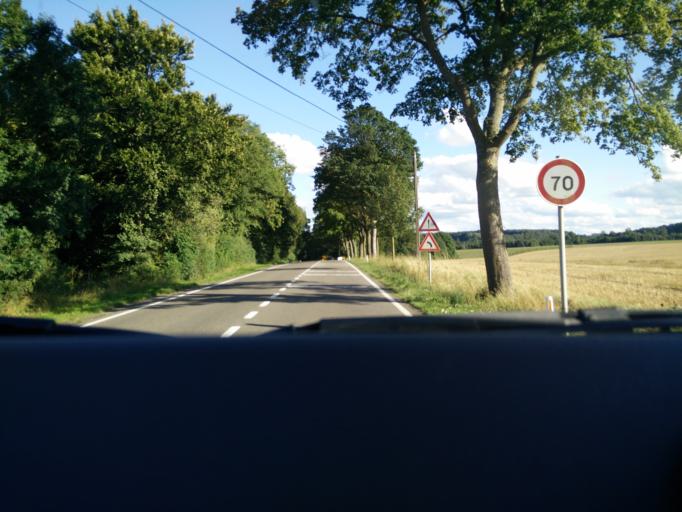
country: BE
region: Wallonia
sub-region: Province du Hainaut
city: Merbes-le-Chateau
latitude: 50.2888
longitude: 4.1753
